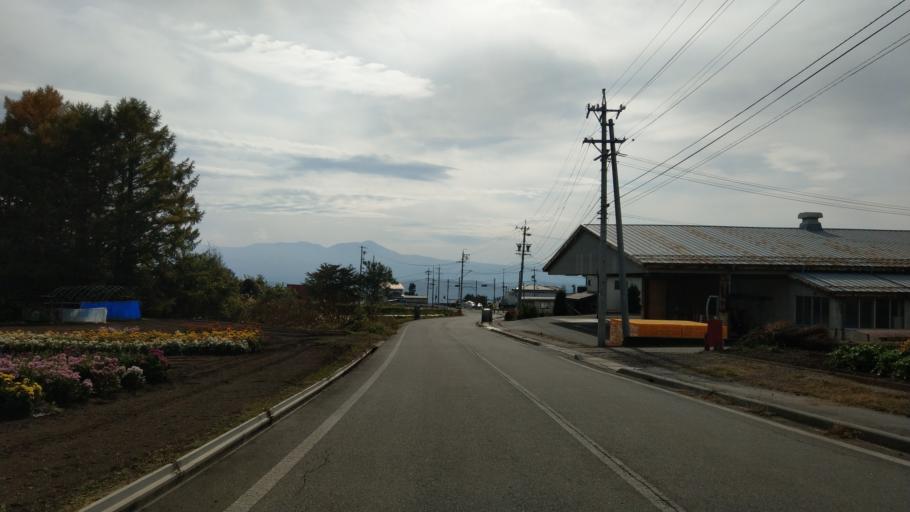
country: JP
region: Nagano
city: Komoro
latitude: 36.3476
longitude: 138.4356
